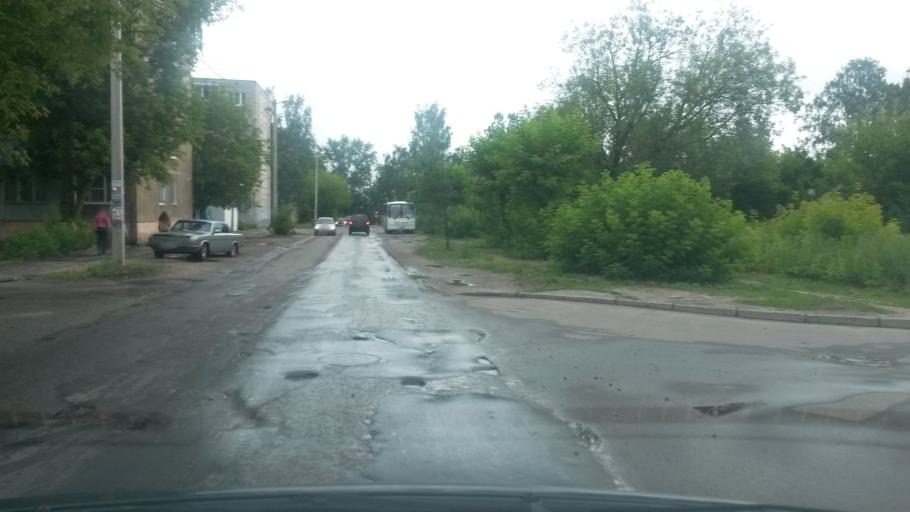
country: RU
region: Ivanovo
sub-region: Gorod Ivanovo
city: Ivanovo
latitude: 57.0051
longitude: 40.9582
